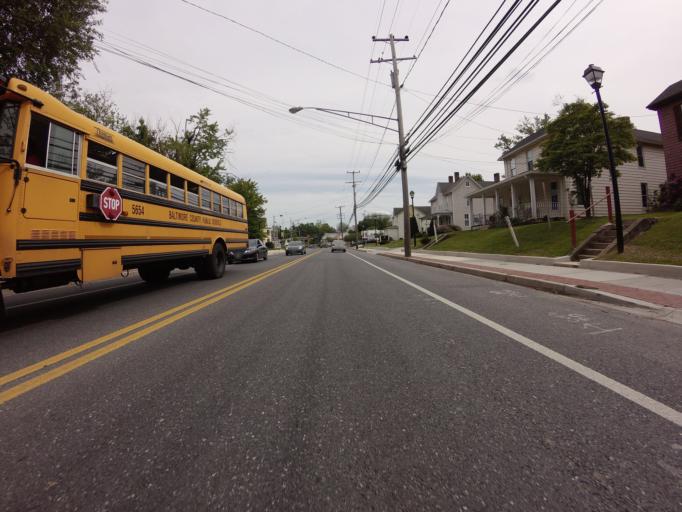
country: US
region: Maryland
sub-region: Baltimore County
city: Reisterstown
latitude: 39.4578
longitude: -76.8268
